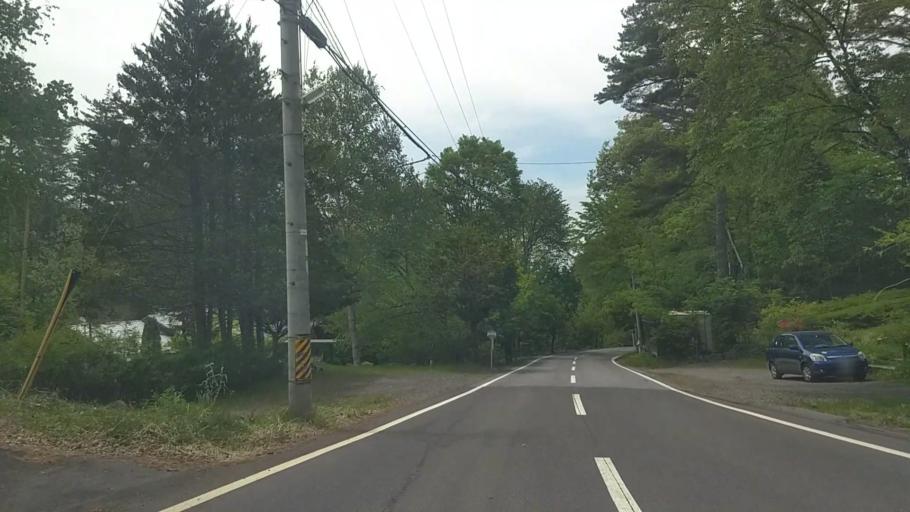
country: JP
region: Nagano
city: Chino
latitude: 36.0343
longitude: 138.2664
